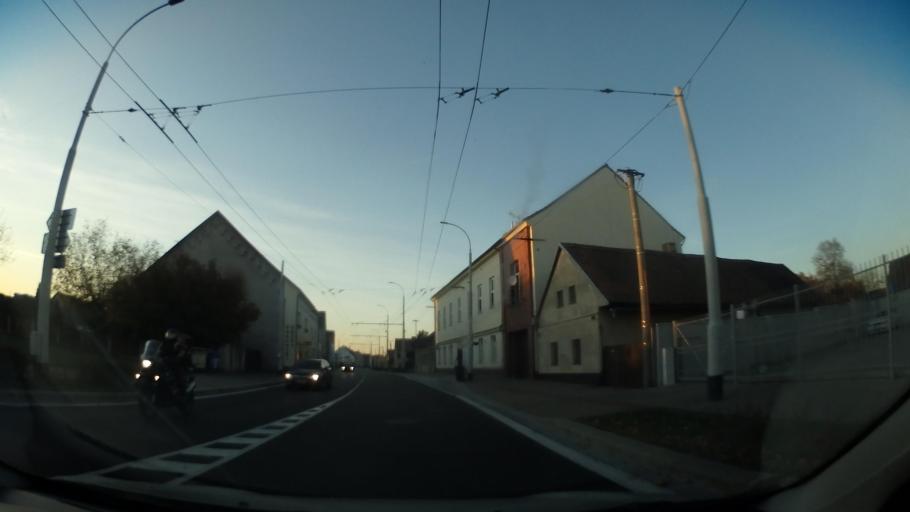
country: CZ
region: Pardubicky
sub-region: Okres Pardubice
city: Lazne Bohdanec
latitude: 50.0766
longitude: 15.6793
